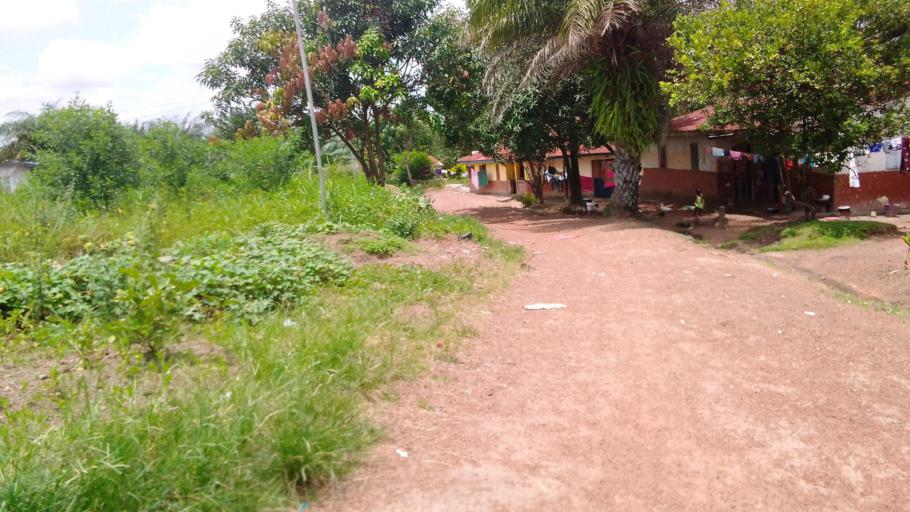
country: SL
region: Northern Province
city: Makeni
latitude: 8.8644
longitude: -12.0378
